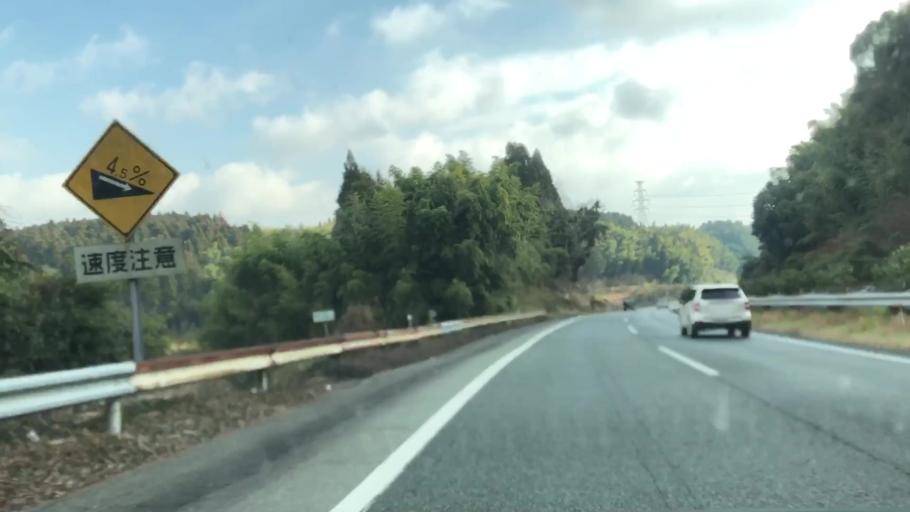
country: JP
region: Kumamoto
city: Yamaga
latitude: 33.0418
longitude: 130.5681
